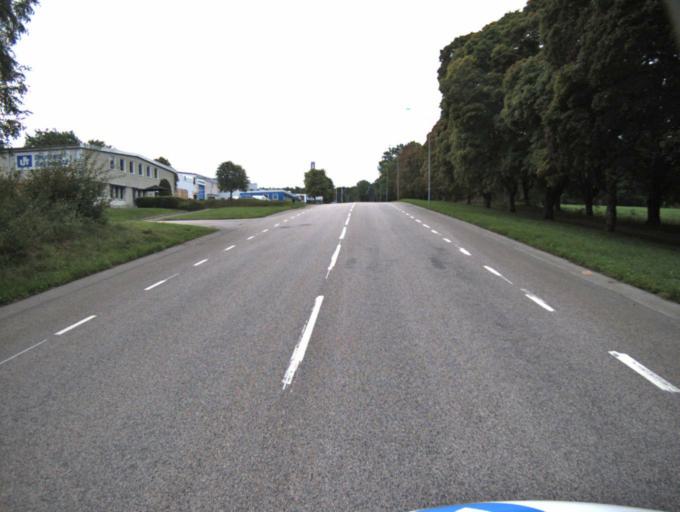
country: SE
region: Vaestra Goetaland
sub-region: Ulricehamns Kommun
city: Ulricehamn
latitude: 57.8024
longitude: 13.4405
